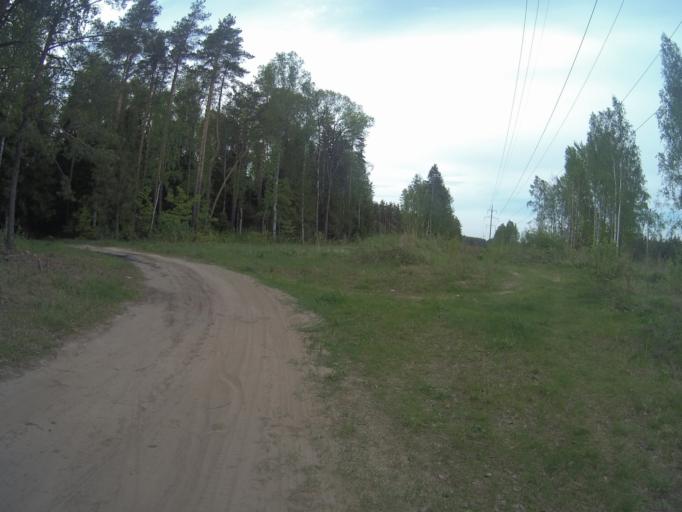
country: RU
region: Vladimir
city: Kommunar
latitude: 56.0486
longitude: 40.4684
